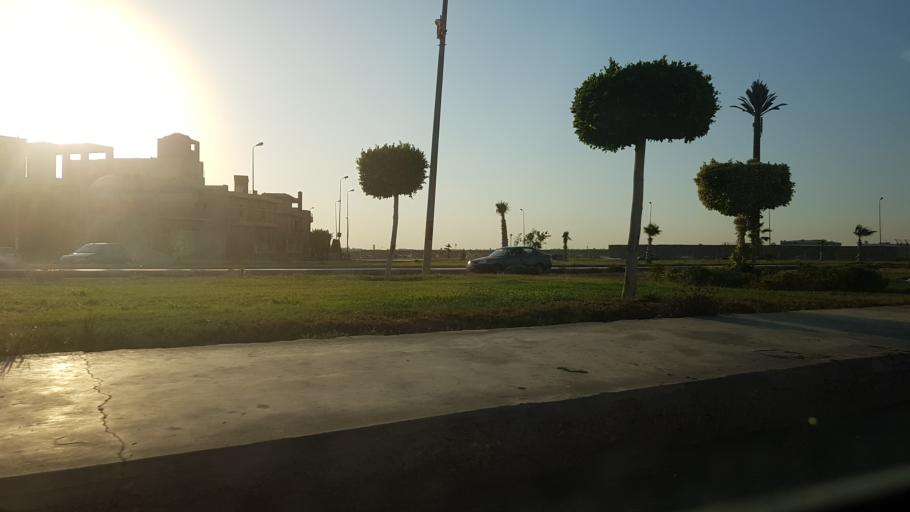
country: EG
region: Muhafazat al Qalyubiyah
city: Al Khankah
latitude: 30.0454
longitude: 31.4421
